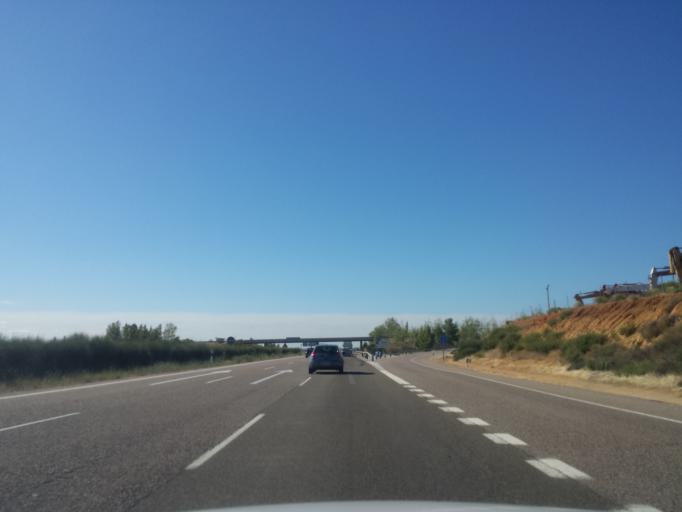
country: ES
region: Castille and Leon
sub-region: Provincia de Zamora
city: Benavente
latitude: 42.0374
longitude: -5.6726
